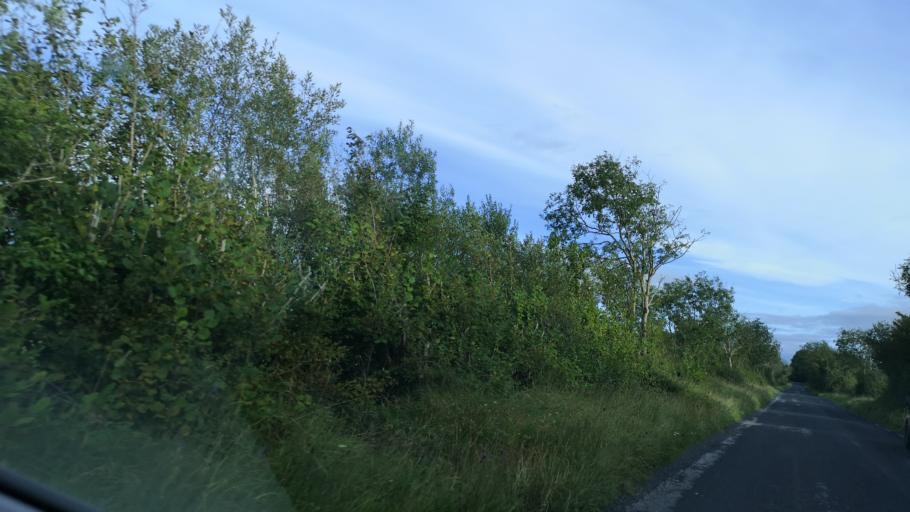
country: IE
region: Connaught
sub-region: County Galway
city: Ballinasloe
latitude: 53.3405
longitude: -8.2923
